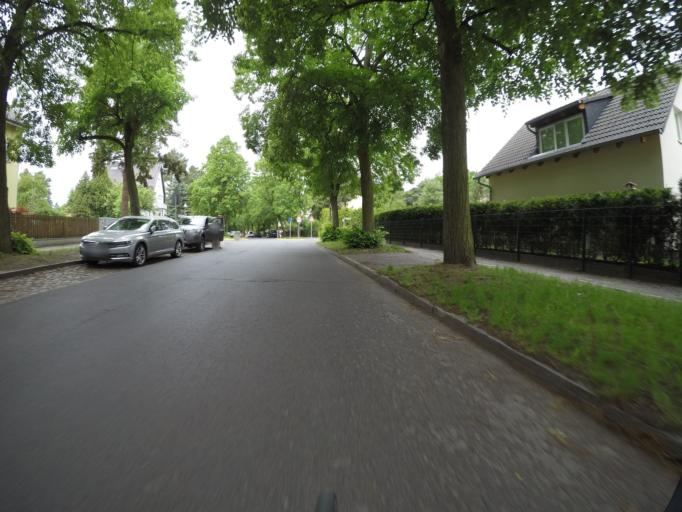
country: DE
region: Brandenburg
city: Glienicke
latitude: 52.6243
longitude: 13.3216
